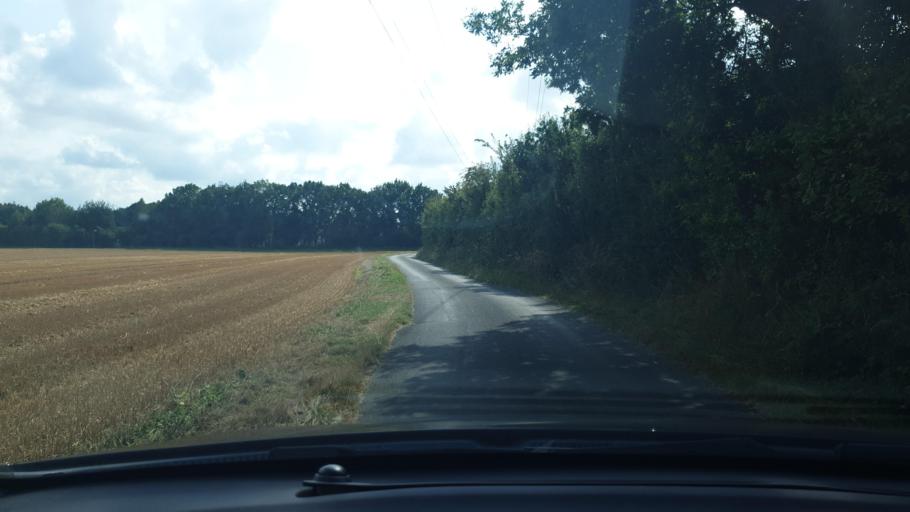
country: GB
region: England
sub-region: Essex
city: Manningtree
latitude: 51.9192
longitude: 1.0192
